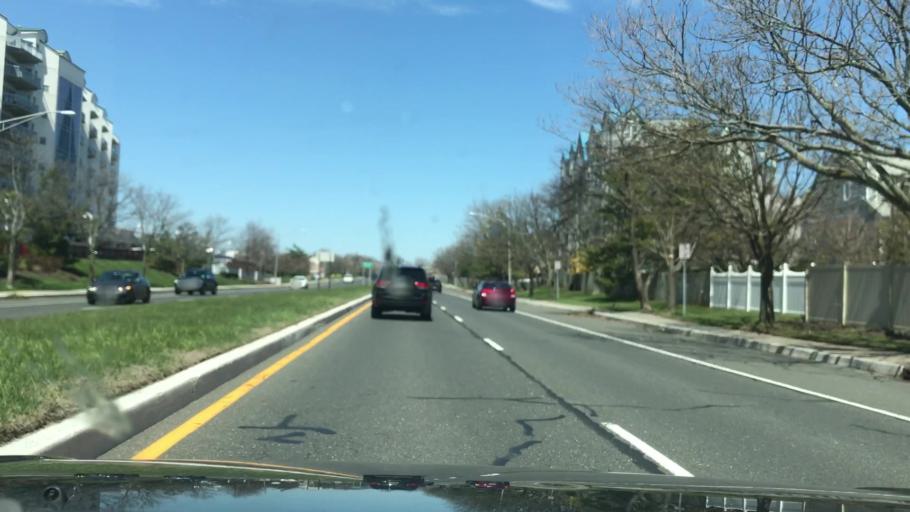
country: US
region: New Jersey
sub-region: Monmouth County
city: Monmouth Beach
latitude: 40.3146
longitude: -73.9800
